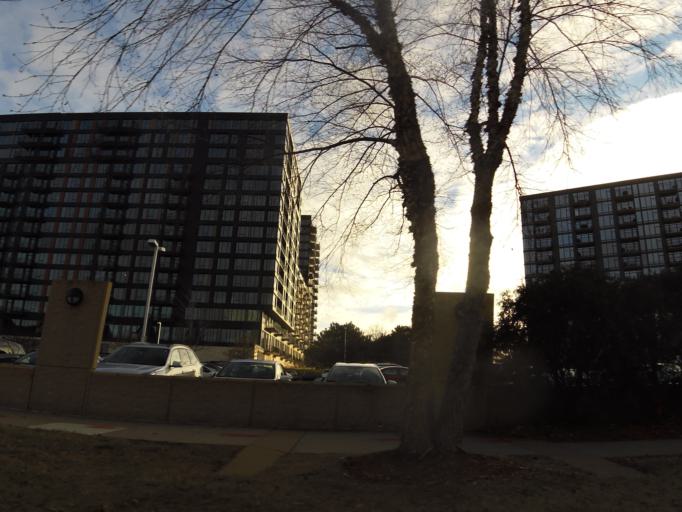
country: US
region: Minnesota
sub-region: Hennepin County
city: Minneapolis
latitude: 44.9775
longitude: -93.2505
